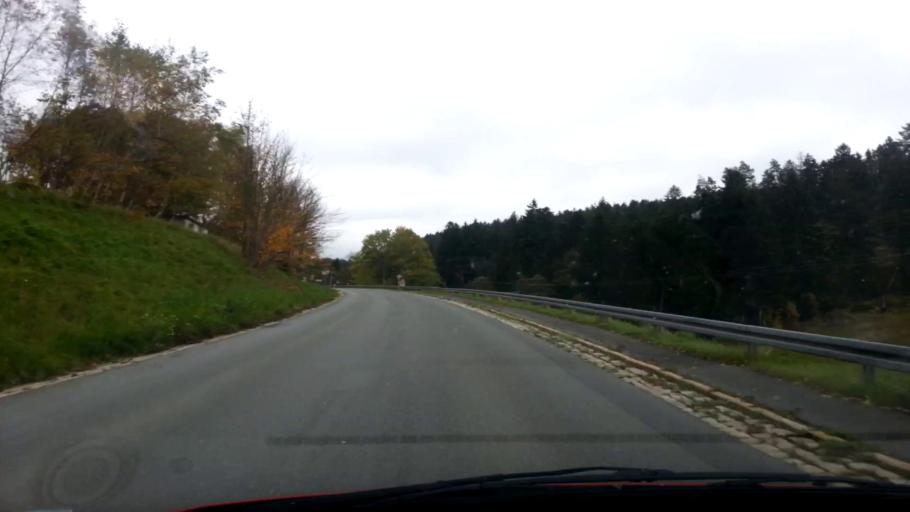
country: DE
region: Bavaria
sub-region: Upper Franconia
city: Warmensteinach
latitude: 50.0021
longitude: 11.8047
